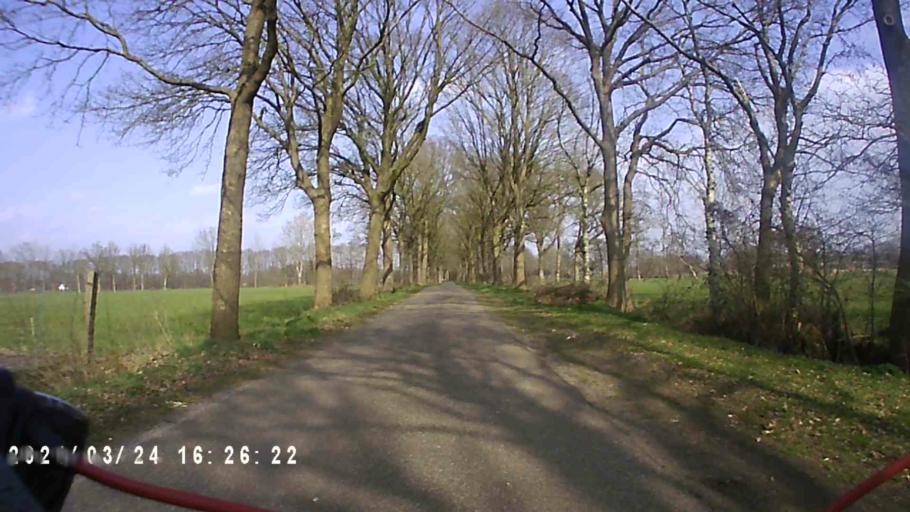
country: NL
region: Friesland
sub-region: Gemeente Smallingerland
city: Drachtstercompagnie
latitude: 53.0637
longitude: 6.2685
